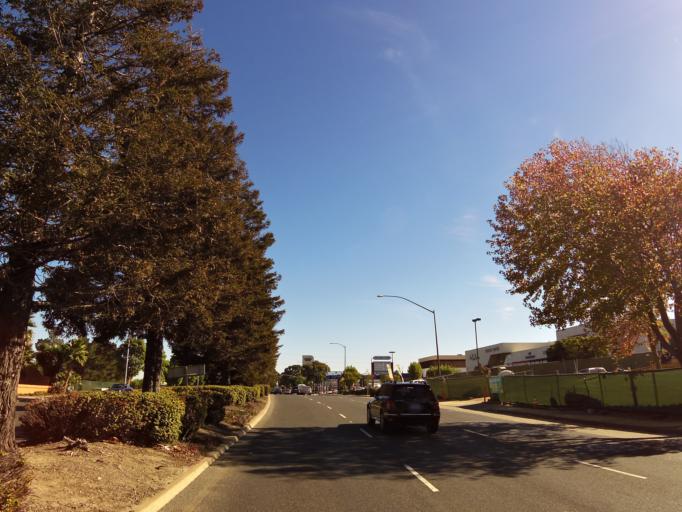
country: US
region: California
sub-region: San Mateo County
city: Millbrae
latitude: 37.6070
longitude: -122.3983
